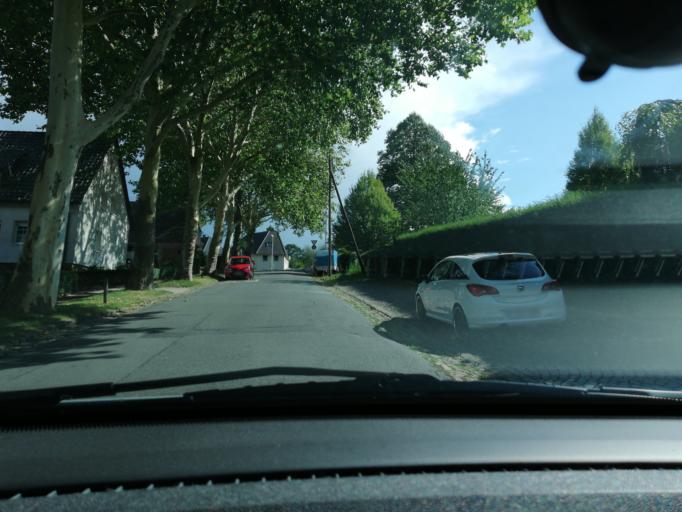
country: DE
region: North Rhine-Westphalia
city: Witten
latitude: 51.4377
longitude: 7.3807
